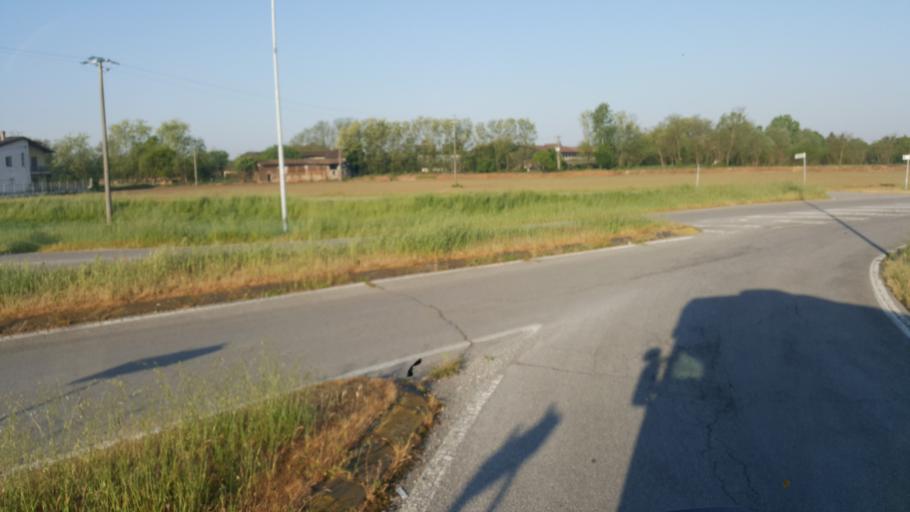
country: IT
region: Lombardy
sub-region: Provincia di Cremona
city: Santa Maria dei Sabbioni
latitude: 45.2383
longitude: 9.8391
